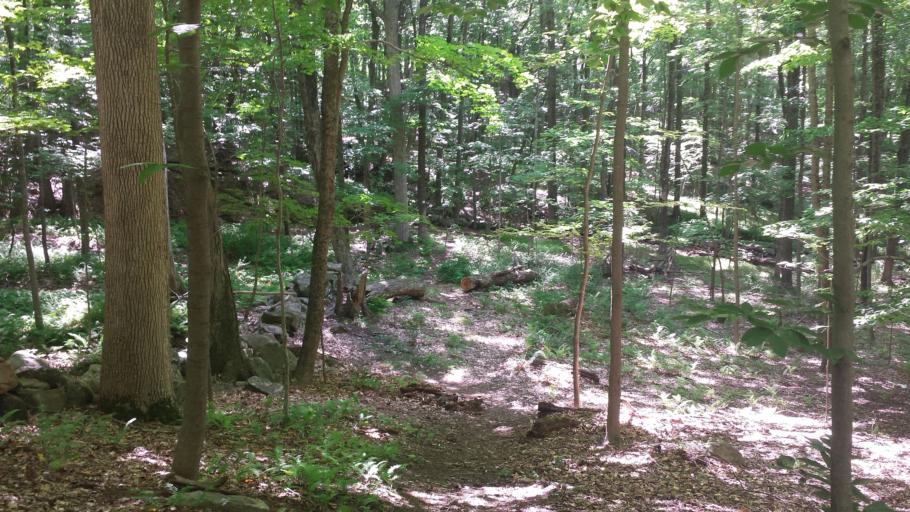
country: US
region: New York
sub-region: Westchester County
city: Pound Ridge
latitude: 41.2588
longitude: -73.5823
